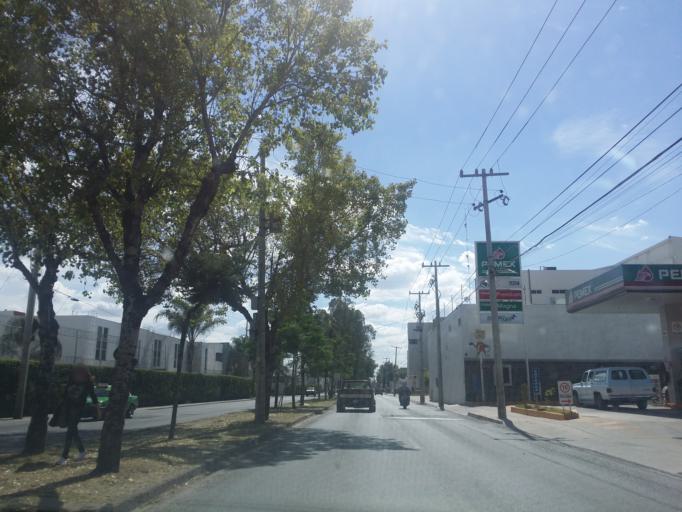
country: MX
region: Guanajuato
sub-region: Leon
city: Medina
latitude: 21.1530
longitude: -101.6469
